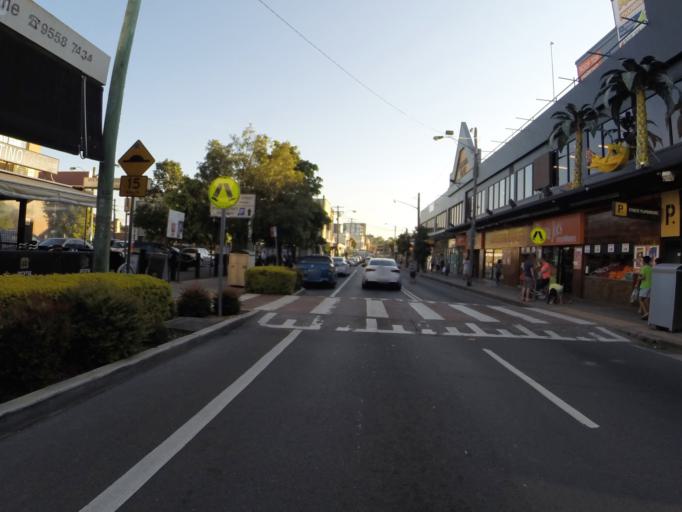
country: AU
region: New South Wales
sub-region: Marrickville
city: Marrickville
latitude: -33.9112
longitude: 151.1556
